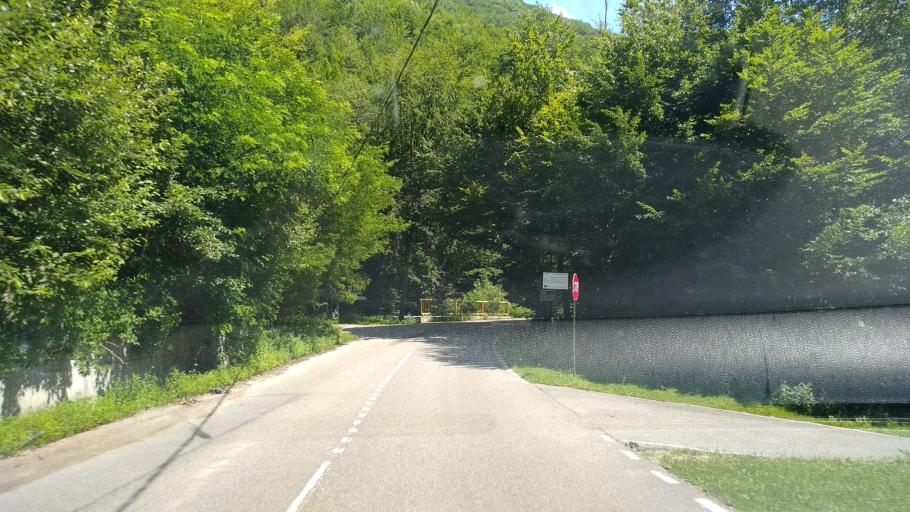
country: RO
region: Hunedoara
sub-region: Comuna Orastioara de Sus
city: Orastioara de Sus
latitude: 45.6548
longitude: 23.1873
